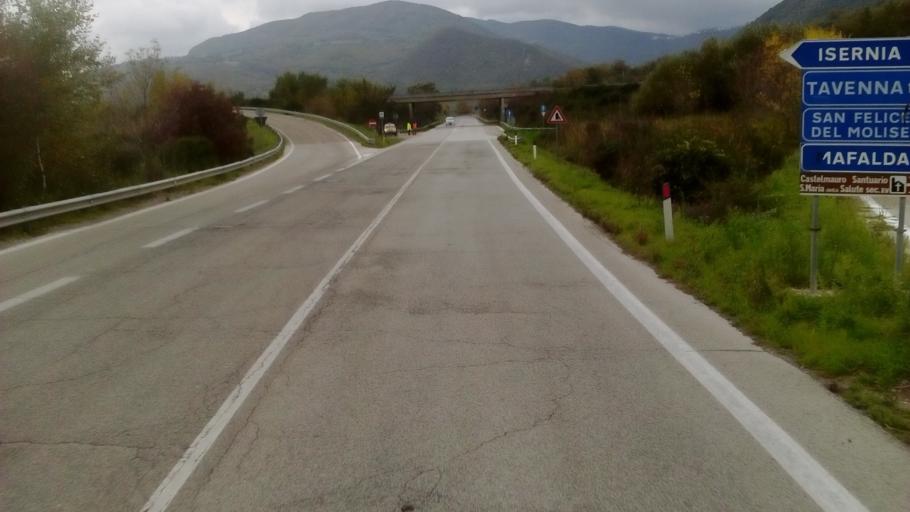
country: IT
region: Abruzzo
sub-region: Provincia di Chieti
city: Dogliola
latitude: 41.9317
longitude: 14.6645
